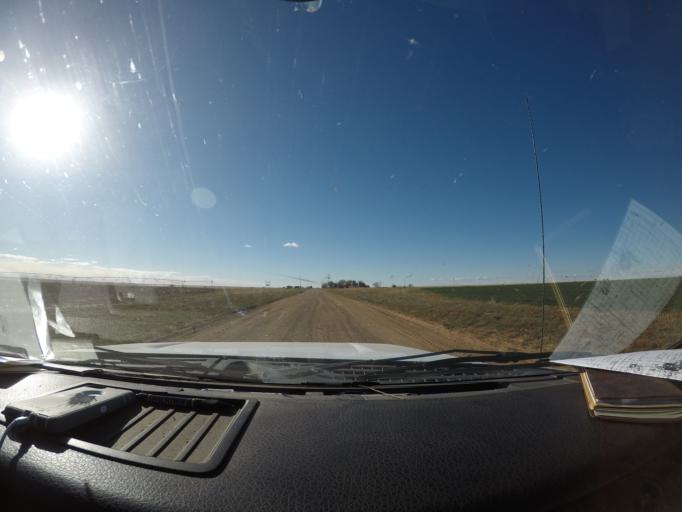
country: US
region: New Mexico
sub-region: Curry County
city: Clovis
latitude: 34.5646
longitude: -103.2304
